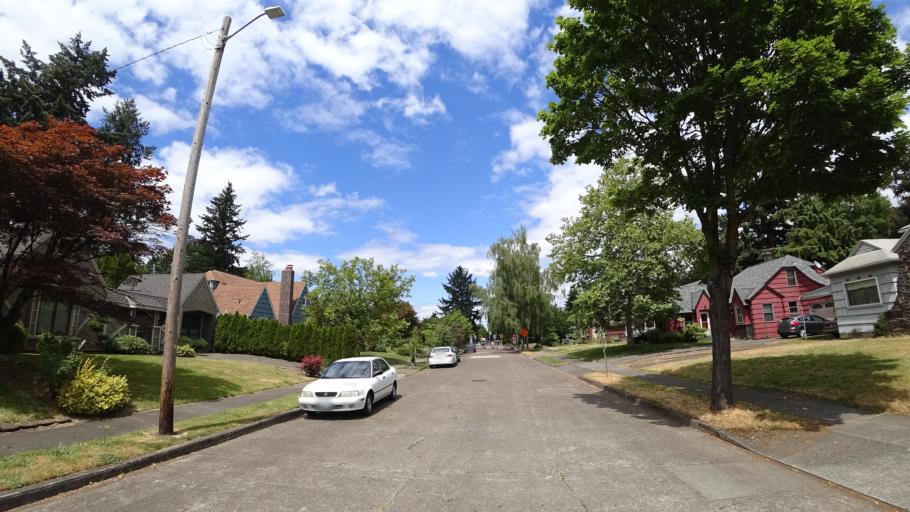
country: US
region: Oregon
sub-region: Multnomah County
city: Portland
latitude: 45.5677
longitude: -122.6760
